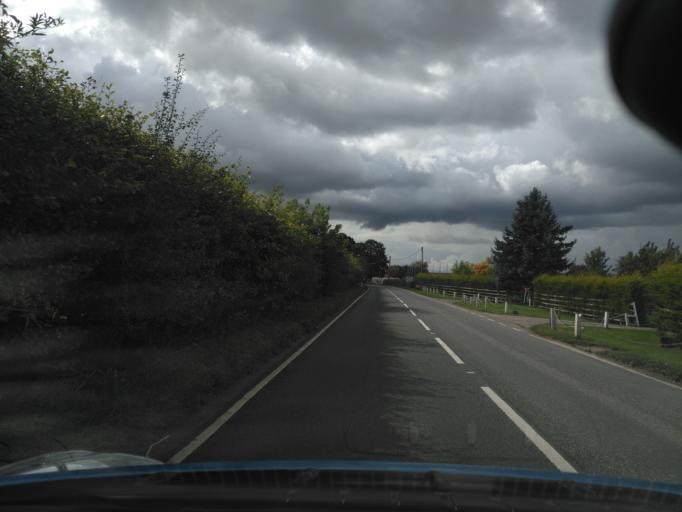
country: GB
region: England
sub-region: Oxfordshire
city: Harwell
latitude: 51.6008
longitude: -1.3323
